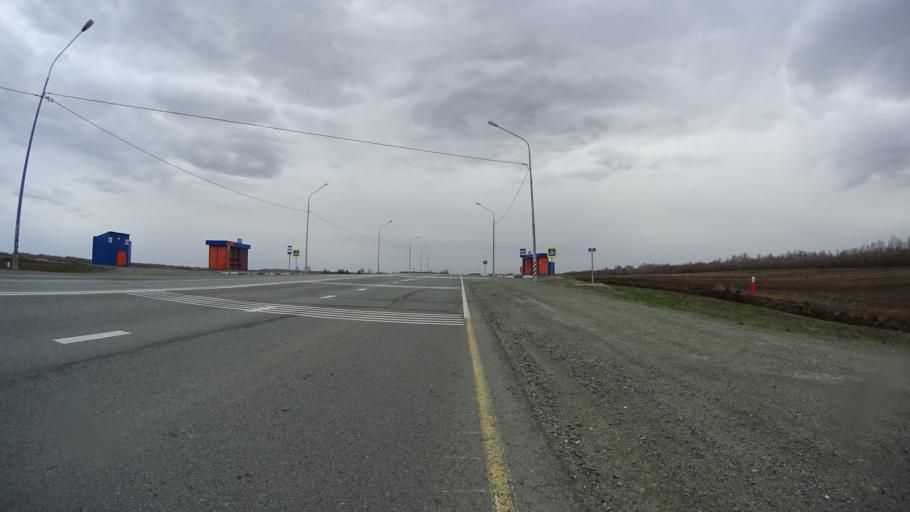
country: RU
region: Chelyabinsk
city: Krasnogorskiy
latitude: 54.6723
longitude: 61.2498
